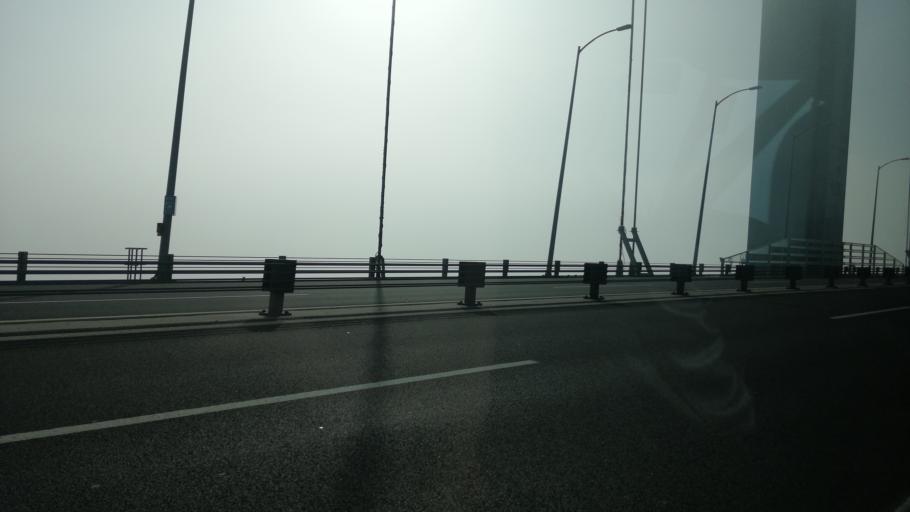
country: TR
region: Kocaeli
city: Tavsancil
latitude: 40.7625
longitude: 29.5169
